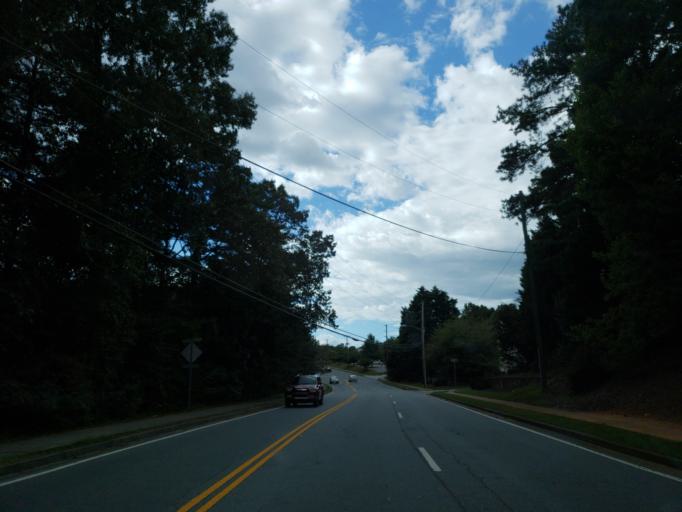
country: US
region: Georgia
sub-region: Cobb County
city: Kennesaw
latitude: 34.0590
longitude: -84.5879
